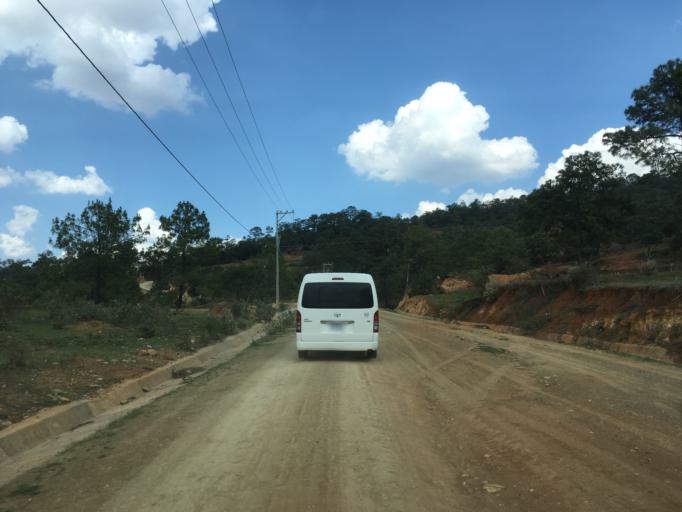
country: MX
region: Oaxaca
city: Santiago Tilantongo
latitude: 17.2181
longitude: -97.2741
